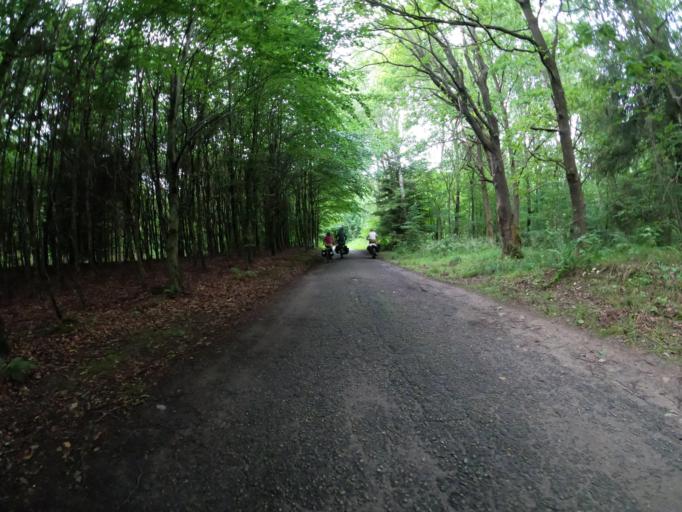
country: PL
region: West Pomeranian Voivodeship
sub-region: Powiat szczecinecki
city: Grzmiaca
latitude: 53.9638
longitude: 16.4480
